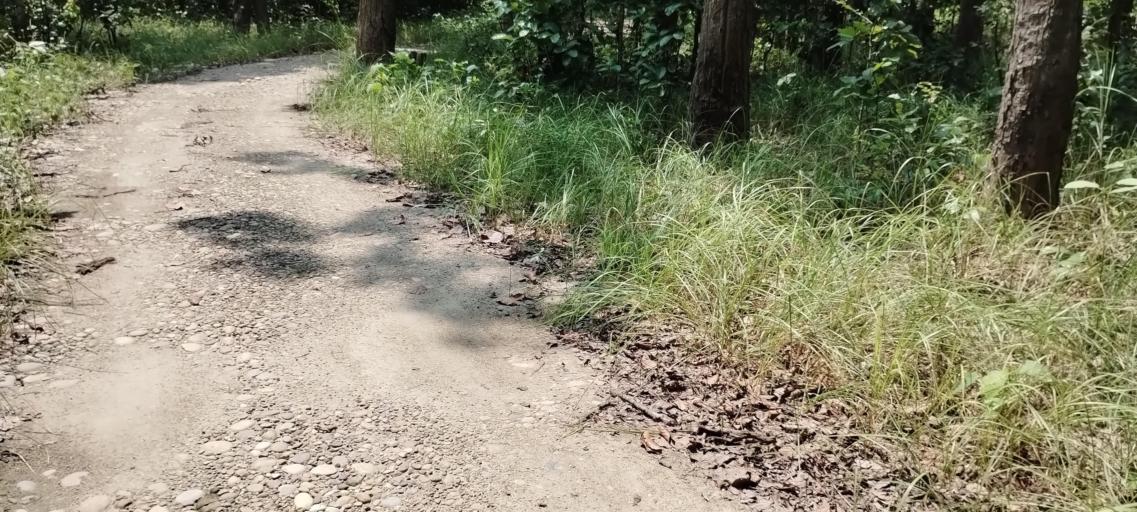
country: NP
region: Far Western
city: Tikapur
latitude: 28.4857
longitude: 81.2578
